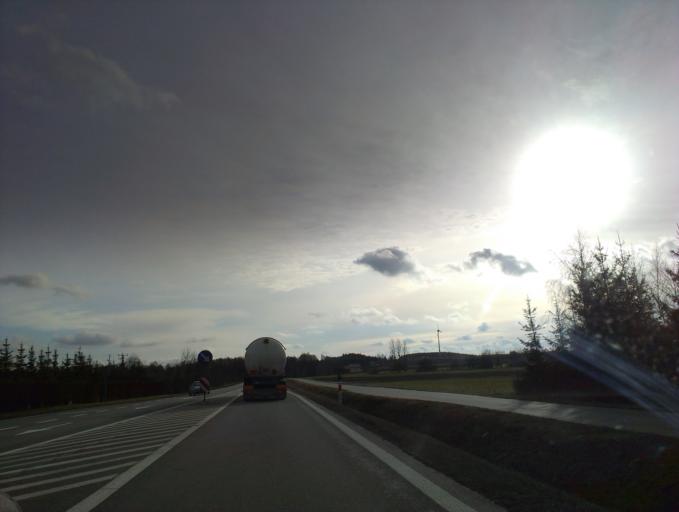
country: PL
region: Kujawsko-Pomorskie
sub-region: Powiat lipnowski
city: Kikol
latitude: 52.9024
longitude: 19.1210
